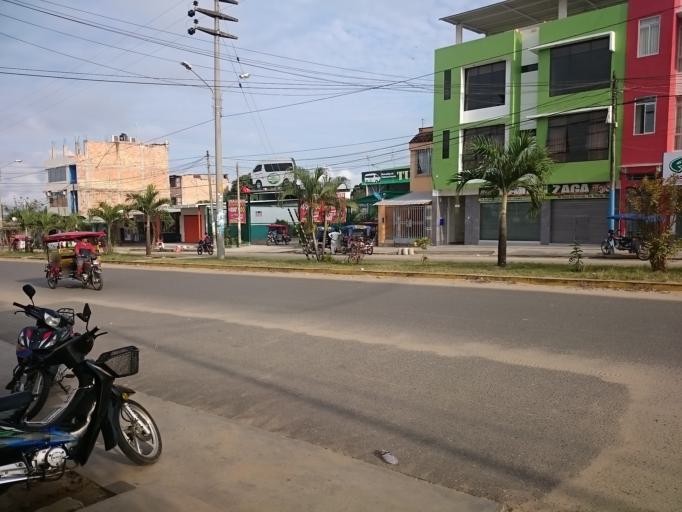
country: PE
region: San Martin
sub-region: Provincia de San Martin
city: Tarapoto
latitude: -6.4918
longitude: -76.3705
